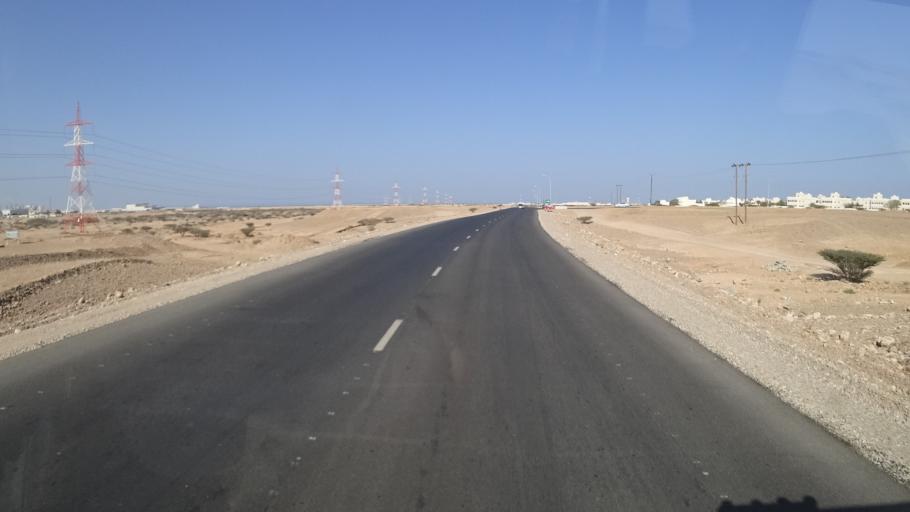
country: OM
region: Ash Sharqiyah
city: Sur
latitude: 22.6067
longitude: 59.4327
